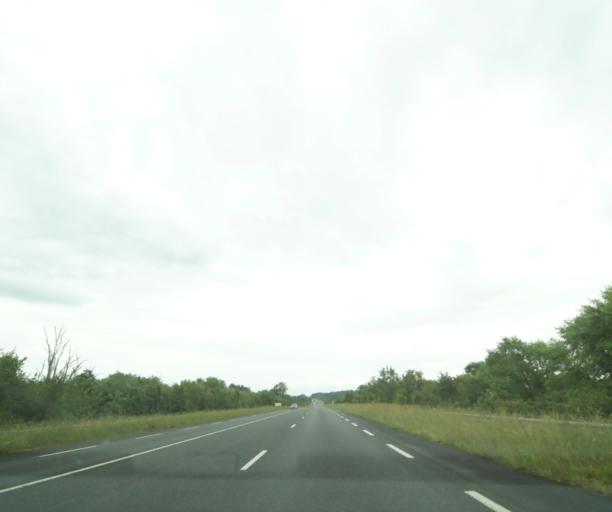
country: FR
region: Poitou-Charentes
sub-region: Departement des Deux-Sevres
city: Airvault
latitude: 46.7820
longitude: -0.2173
